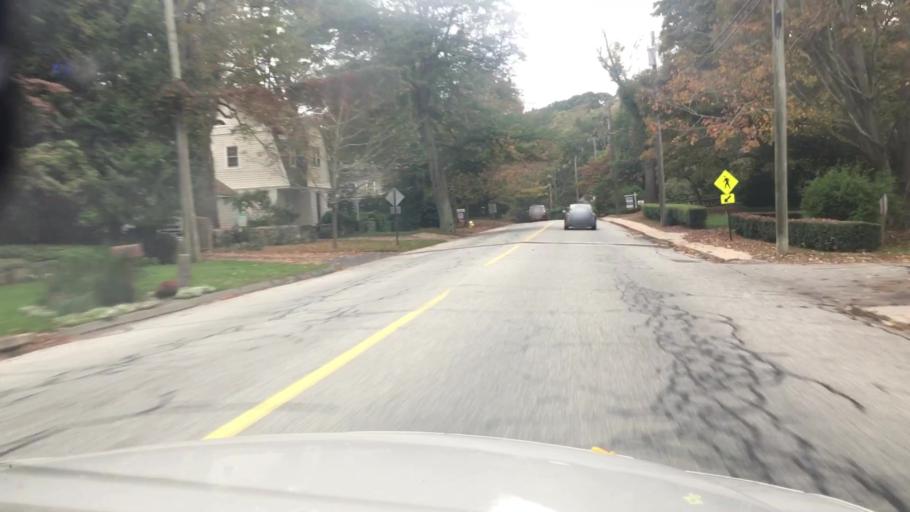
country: US
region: Connecticut
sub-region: Middlesex County
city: Essex Village
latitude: 41.3539
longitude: -72.3969
